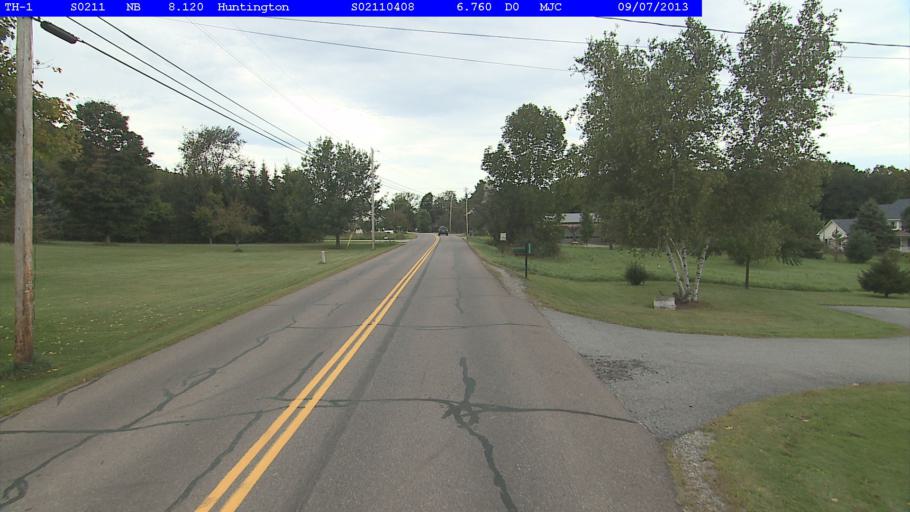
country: US
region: Vermont
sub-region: Chittenden County
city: Hinesburg
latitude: 44.3162
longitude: -72.9890
